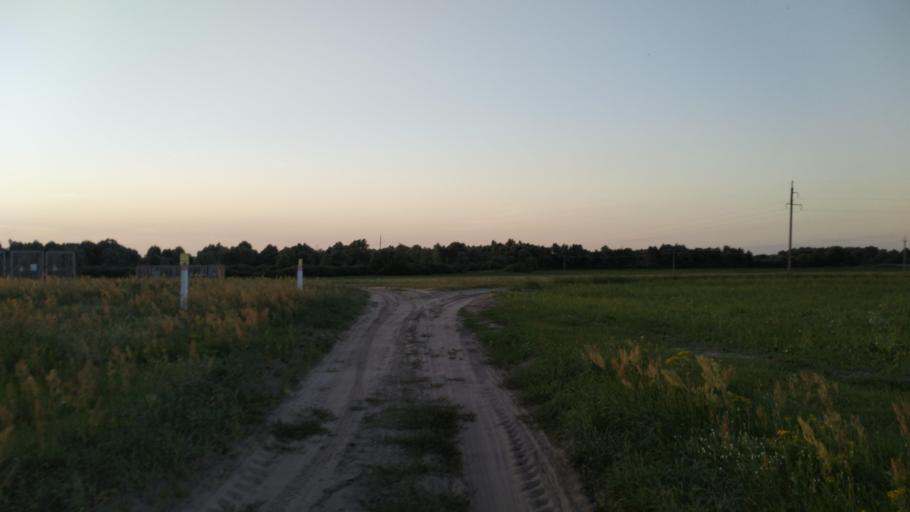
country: BY
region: Brest
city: Davyd-Haradok
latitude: 52.0337
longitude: 27.1931
